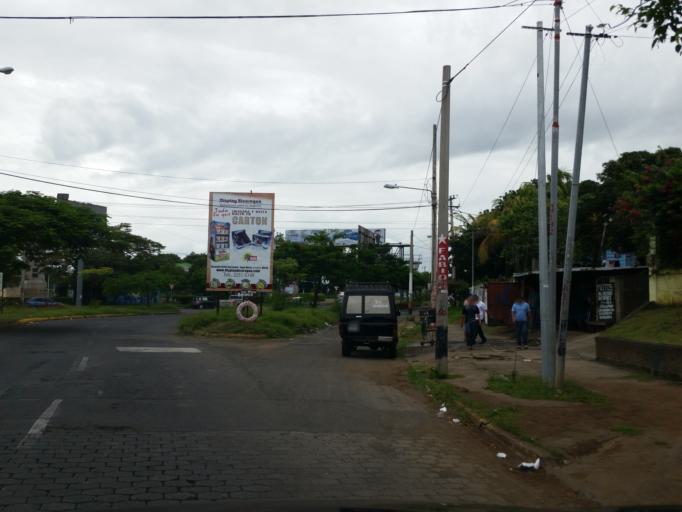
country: NI
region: Managua
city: Managua
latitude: 12.1435
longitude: -86.2260
